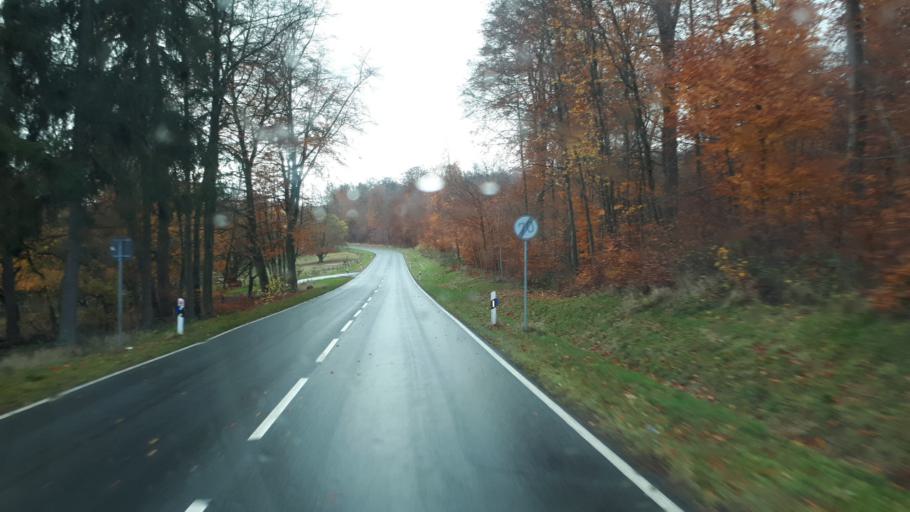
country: DE
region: Rheinland-Pfalz
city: Kaisersesch
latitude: 50.2250
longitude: 7.1283
